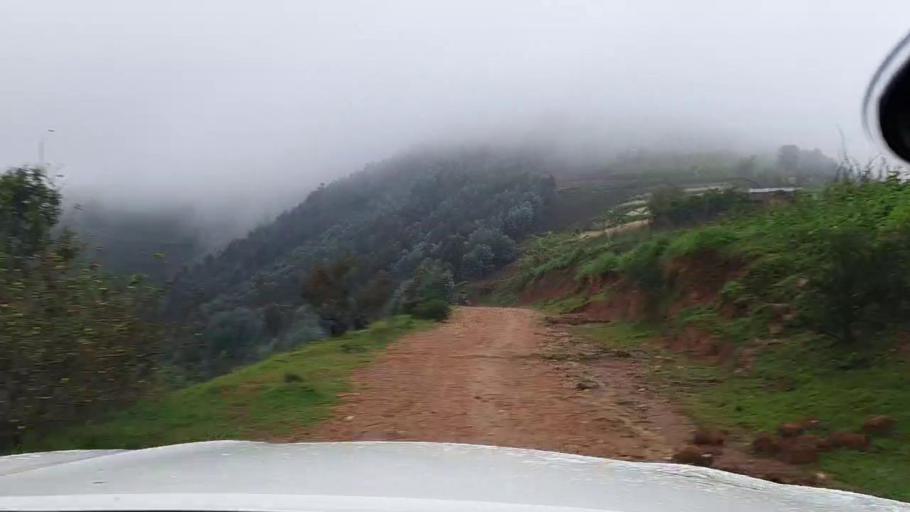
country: RW
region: Western Province
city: Kibuye
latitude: -2.1415
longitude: 29.4599
